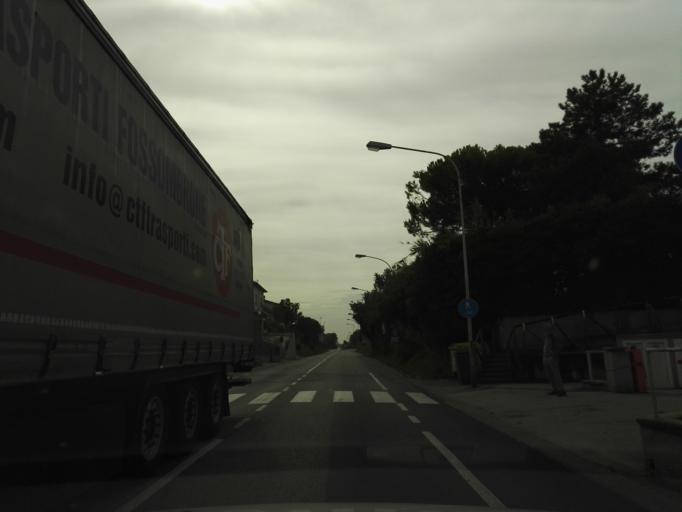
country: IT
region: The Marches
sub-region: Provincia di Pesaro e Urbino
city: Marotta
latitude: 43.7673
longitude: 13.1397
